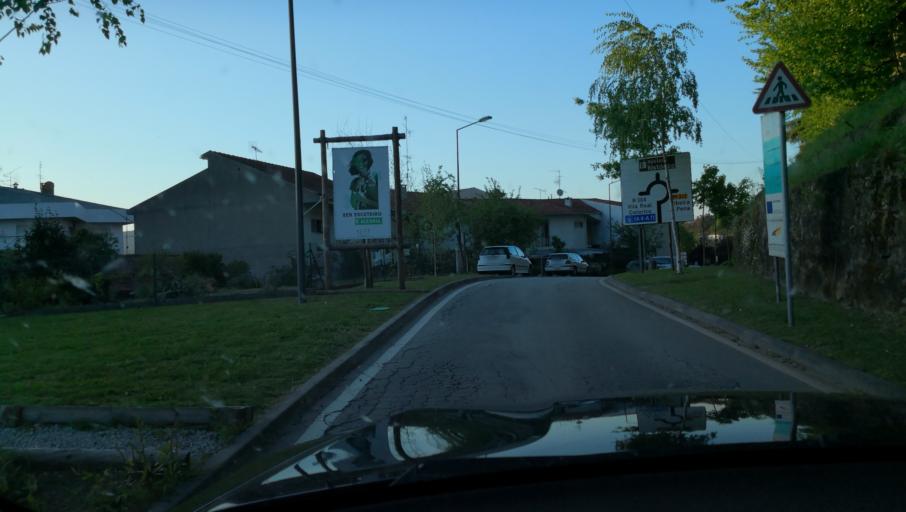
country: PT
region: Vila Real
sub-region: Mondim de Basto
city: Mondim de Basto
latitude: 41.4095
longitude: -7.9520
